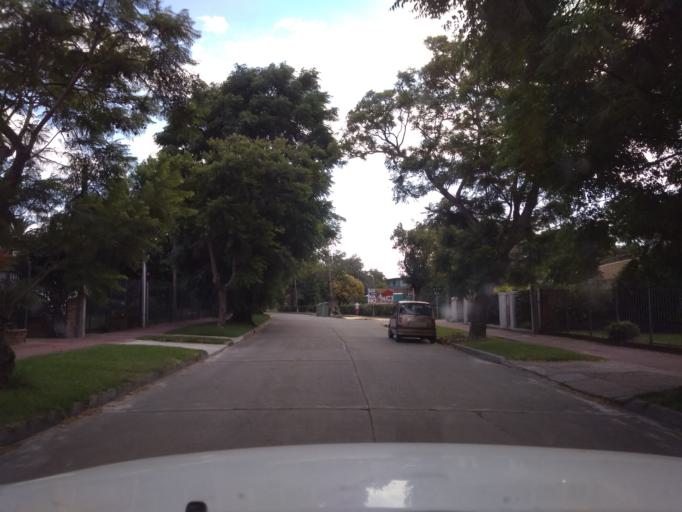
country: UY
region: Canelones
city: Paso de Carrasco
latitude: -34.8863
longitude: -56.0833
